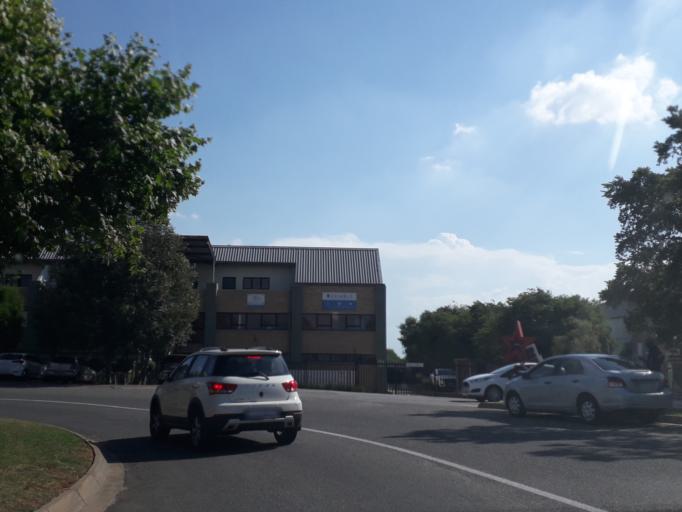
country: ZA
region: Gauteng
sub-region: City of Johannesburg Metropolitan Municipality
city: Midrand
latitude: -25.9409
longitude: 28.1415
